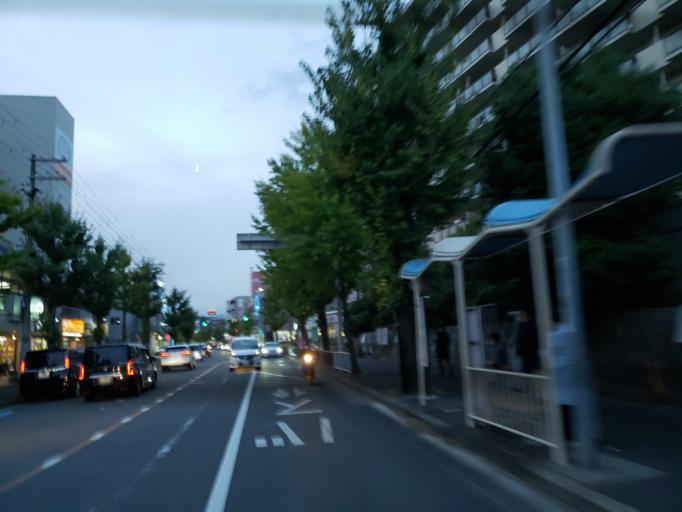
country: JP
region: Osaka
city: Suita
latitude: 34.7893
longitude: 135.5287
